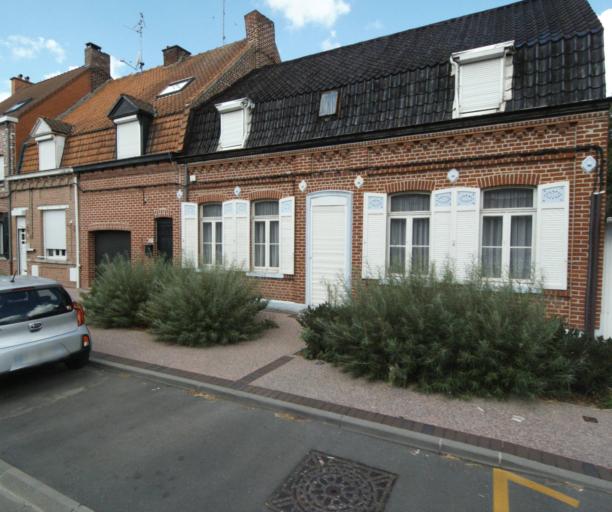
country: FR
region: Nord-Pas-de-Calais
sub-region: Departement du Nord
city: Willems
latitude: 50.6324
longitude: 3.2360
